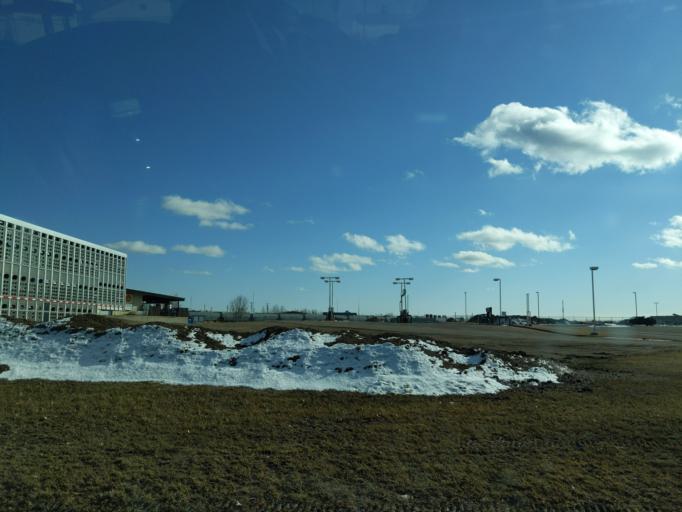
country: CA
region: Saskatchewan
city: Lloydminster
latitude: 53.2866
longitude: -110.0362
